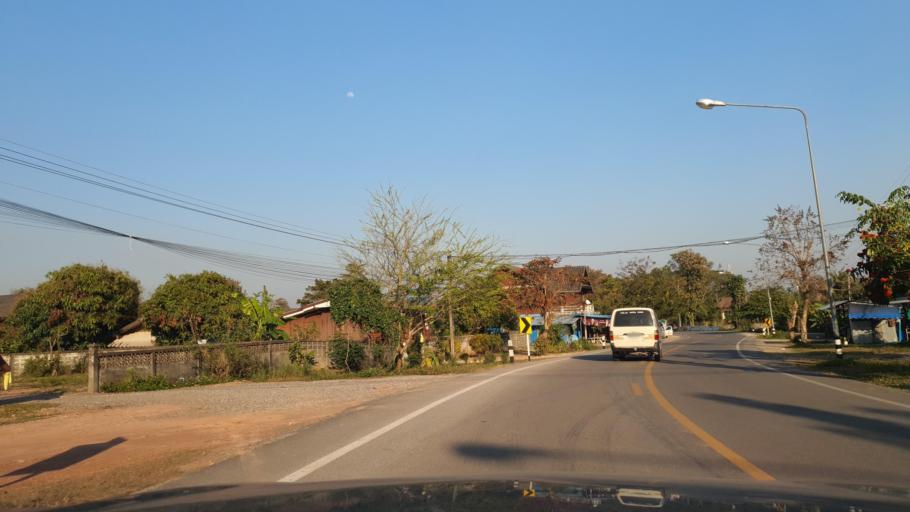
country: TH
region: Chiang Rai
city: Mae Lao
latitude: 19.8347
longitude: 99.6955
